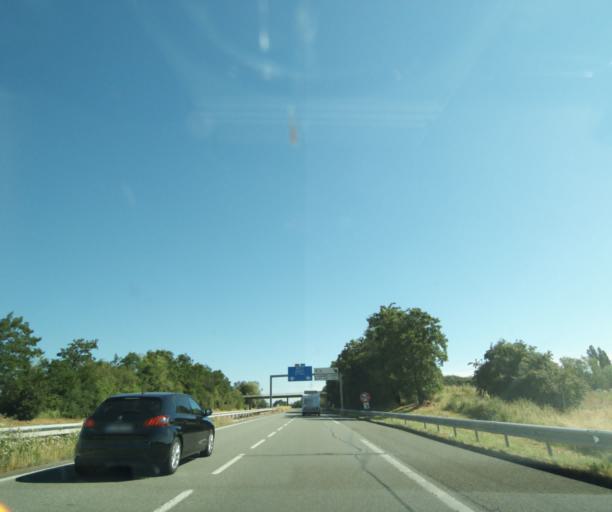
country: FR
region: Champagne-Ardenne
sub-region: Departement de la Haute-Marne
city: Avrecourt
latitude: 47.9908
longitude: 5.5114
